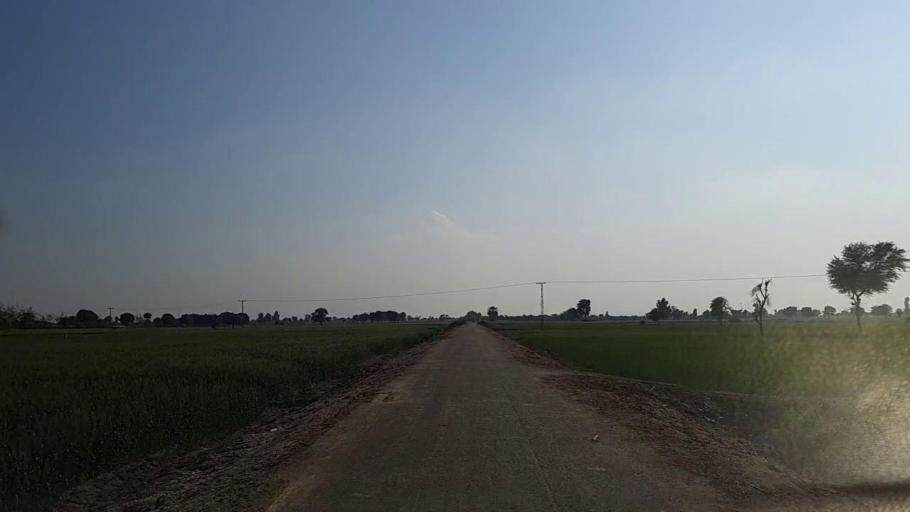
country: PK
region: Sindh
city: Jam Sahib
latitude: 26.2848
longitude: 68.6137
